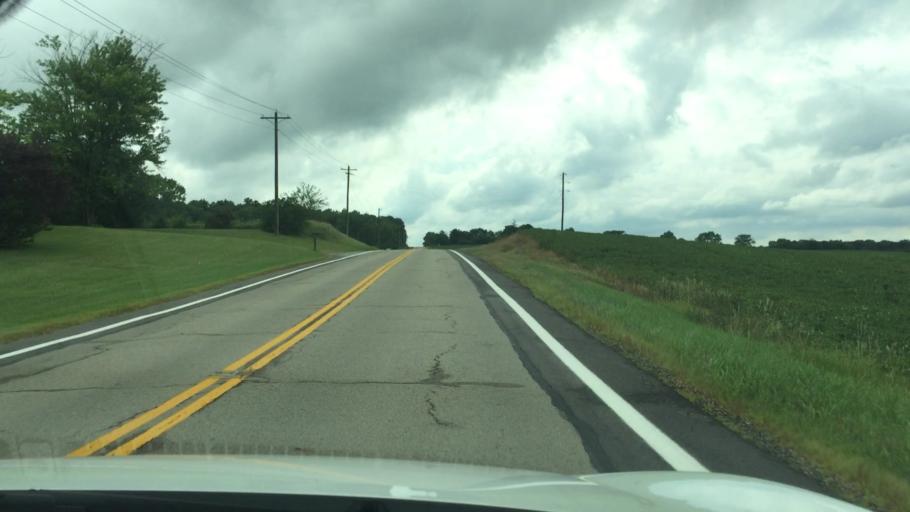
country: US
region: Ohio
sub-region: Champaign County
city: Mechanicsburg
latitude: 40.0881
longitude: -83.6114
